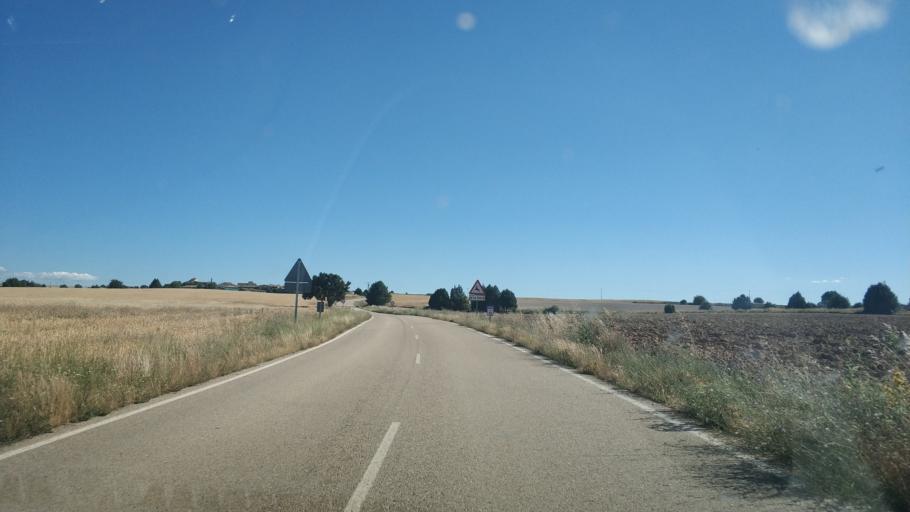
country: ES
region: Castille and Leon
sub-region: Provincia de Soria
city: Liceras
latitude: 41.4726
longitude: -3.2158
